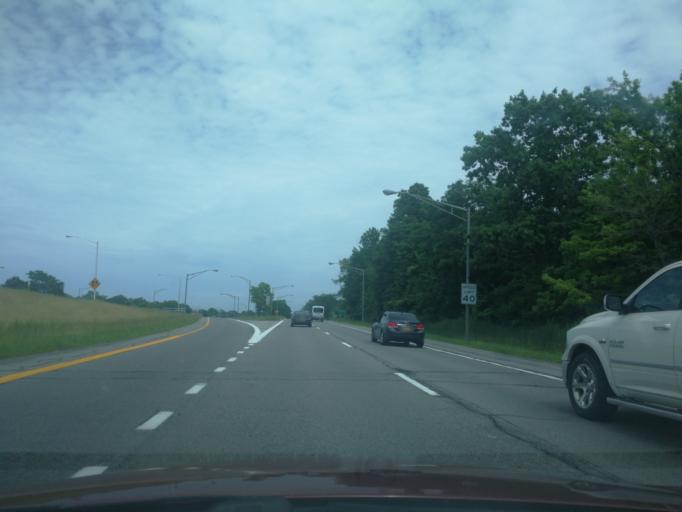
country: US
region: New York
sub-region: Monroe County
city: Irondequoit
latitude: 43.1932
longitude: -77.5910
